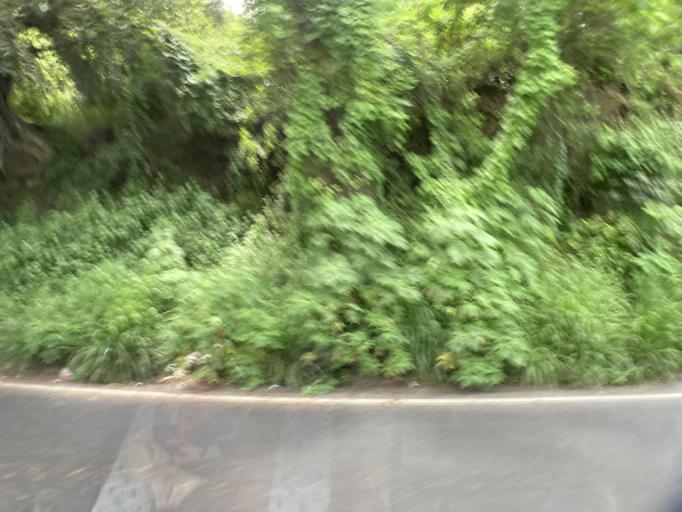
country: GT
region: Guatemala
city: Amatitlan
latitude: 14.4955
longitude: -90.6239
